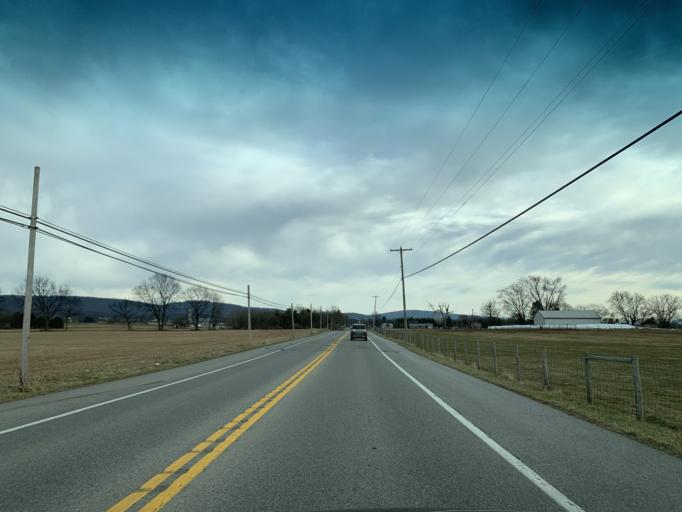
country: US
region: Maryland
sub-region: Washington County
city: Boonsboro
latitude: 39.5393
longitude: -77.6723
